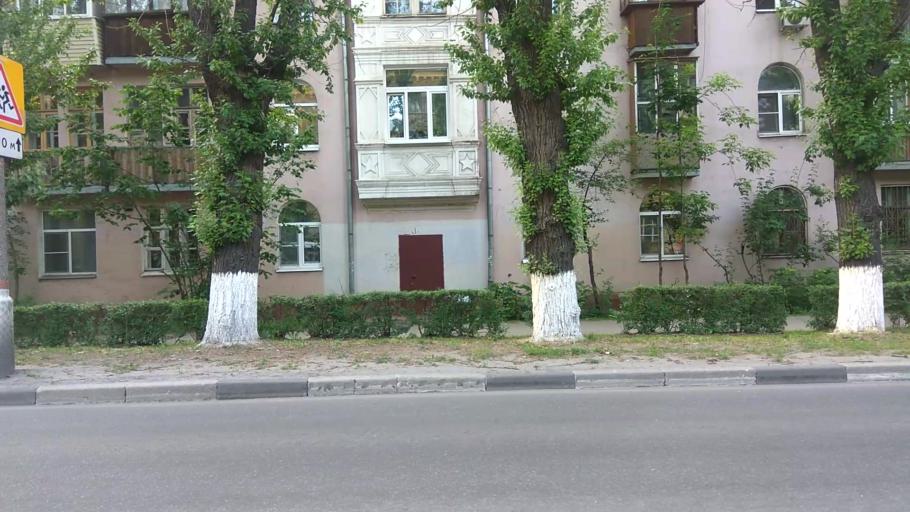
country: RU
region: Moskovskaya
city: Korolev
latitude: 55.9206
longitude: 37.8217
